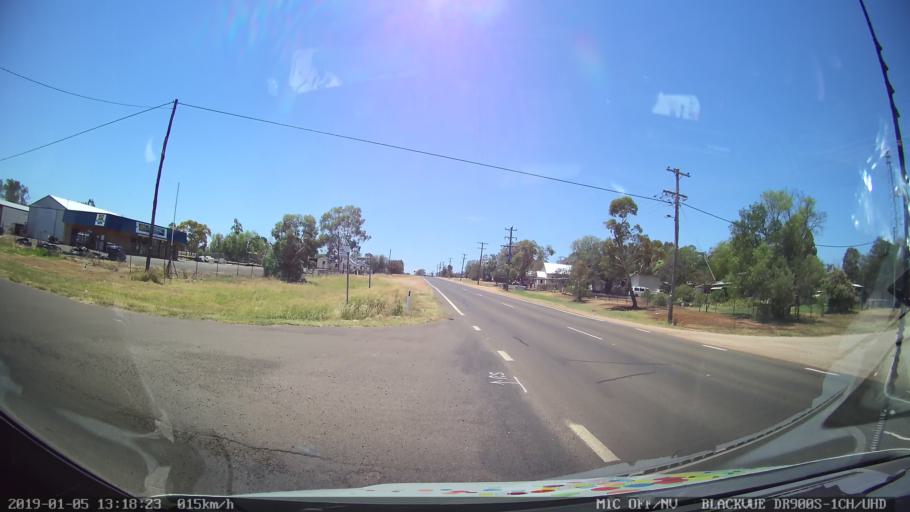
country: AU
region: New South Wales
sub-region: Gunnedah
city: Gunnedah
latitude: -31.0976
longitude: 149.9106
